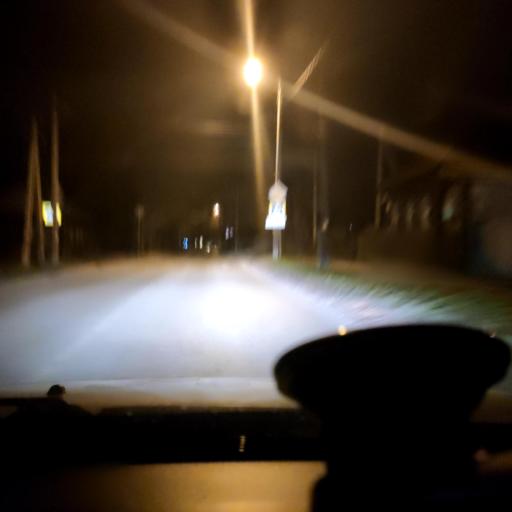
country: RU
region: Perm
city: Perm
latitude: 58.0286
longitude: 56.3300
